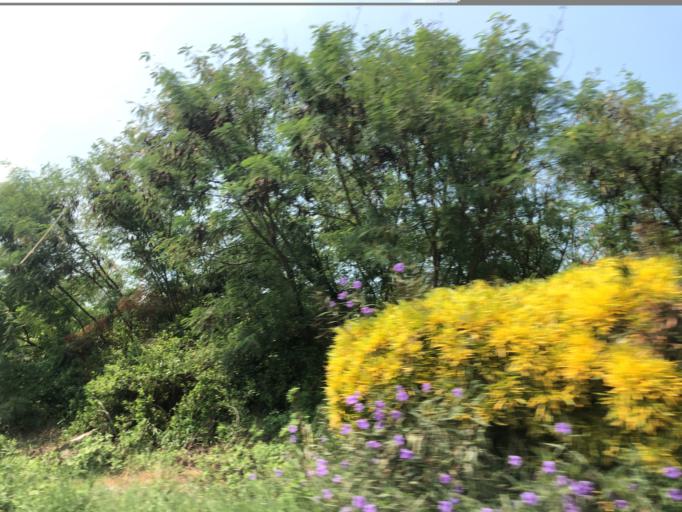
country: TW
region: Taiwan
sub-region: Chiayi
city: Taibao
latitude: 23.4598
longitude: 120.1509
